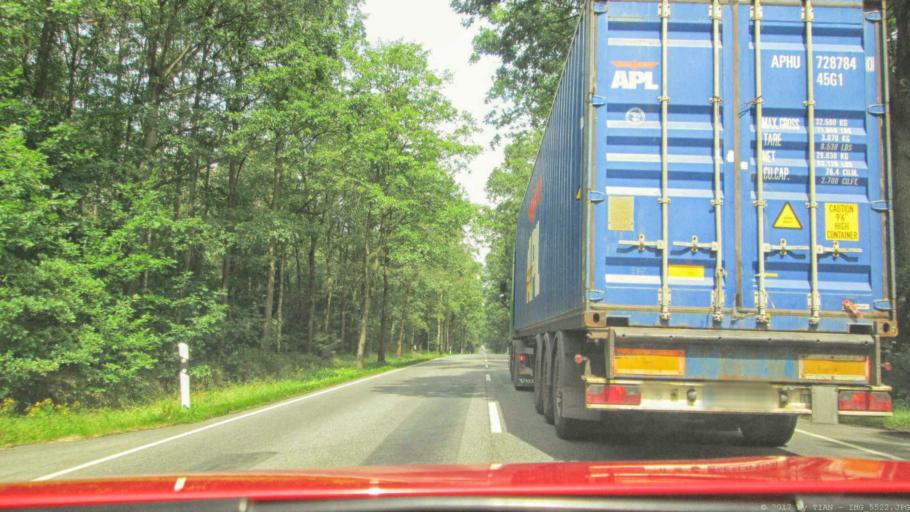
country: DE
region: Lower Saxony
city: Sprakensehl
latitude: 52.7915
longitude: 10.4899
